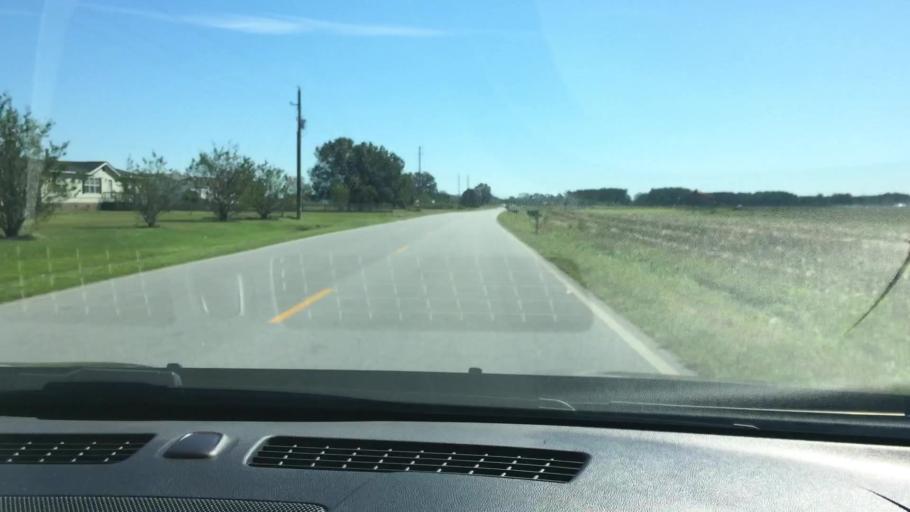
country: US
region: North Carolina
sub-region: Pitt County
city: Grifton
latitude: 35.3863
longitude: -77.3803
